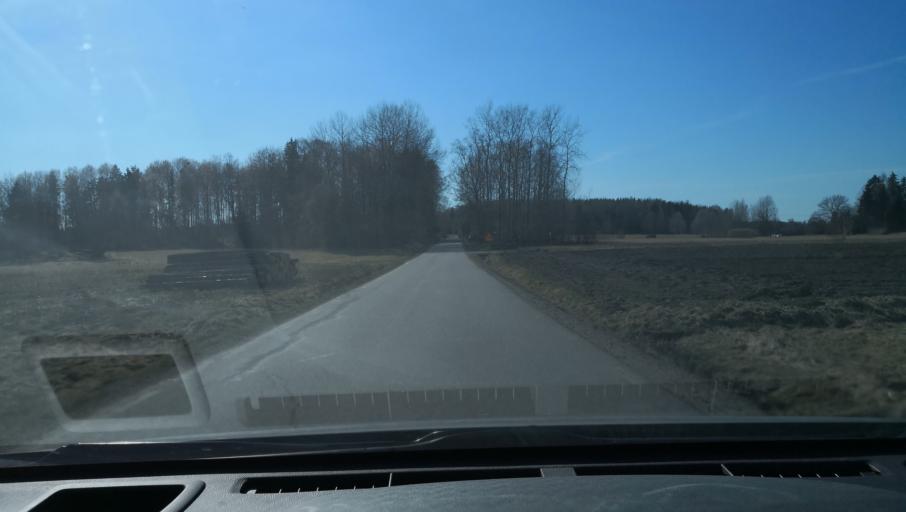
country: SE
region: Vaestmanland
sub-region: Sala Kommun
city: Sala
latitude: 60.0859
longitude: 16.5185
